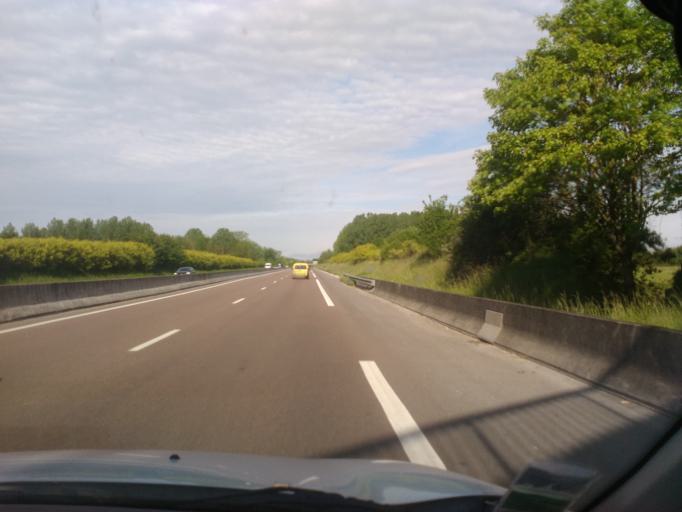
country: FR
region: Champagne-Ardenne
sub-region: Departement de l'Aube
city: Sainte-Maure
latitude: 48.3278
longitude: 4.0668
